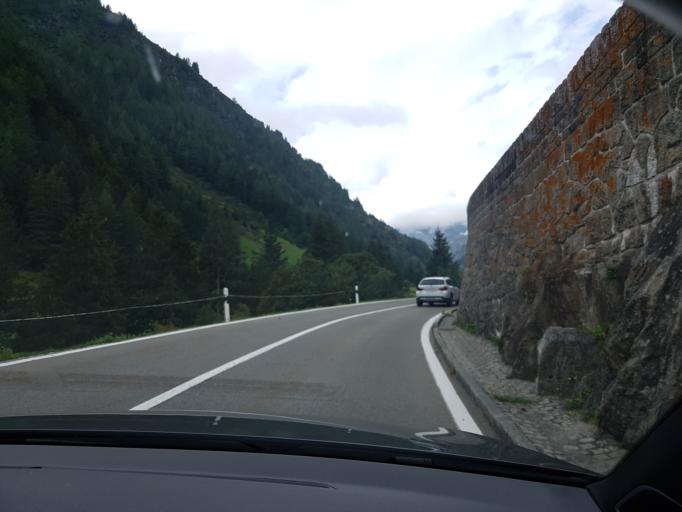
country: CH
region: Uri
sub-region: Uri
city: Andermatt
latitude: 46.7250
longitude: 8.5532
